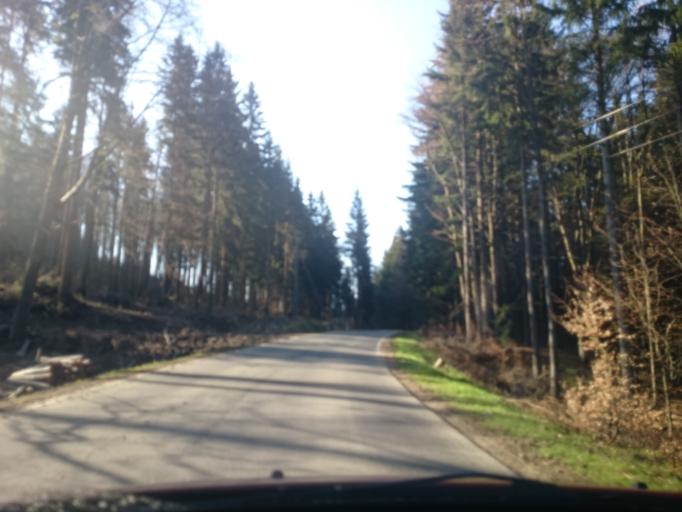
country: PL
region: Lower Silesian Voivodeship
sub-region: Powiat klodzki
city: Duszniki-Zdroj
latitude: 50.3253
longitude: 16.4117
